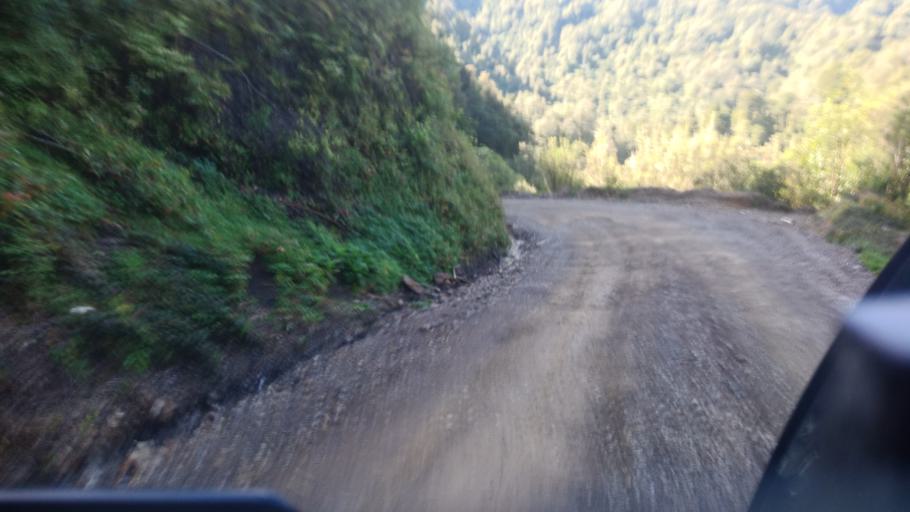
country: NZ
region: Bay of Plenty
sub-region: Opotiki District
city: Opotiki
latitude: -38.0613
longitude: 177.4640
